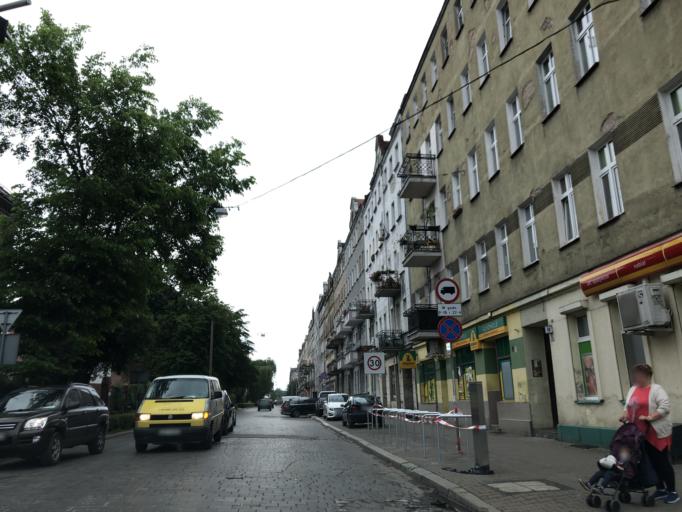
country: PL
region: Lower Silesian Voivodeship
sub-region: Powiat wroclawski
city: Wroclaw
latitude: 51.1269
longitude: 17.0278
